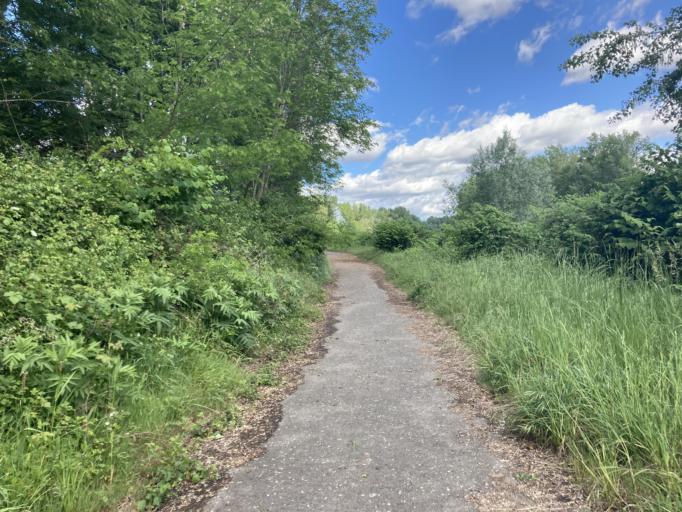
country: FR
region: Aquitaine
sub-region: Departement des Pyrenees-Atlantiques
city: Arbus
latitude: 43.3401
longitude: -0.5014
